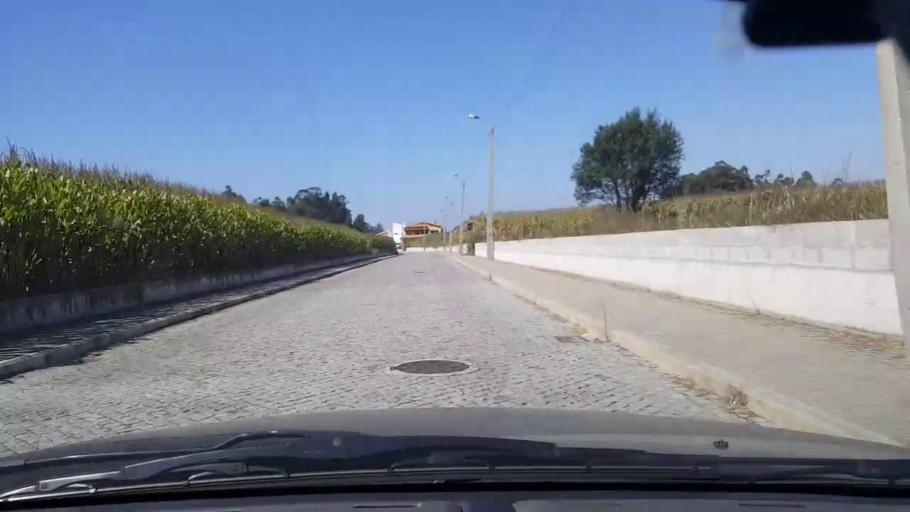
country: PT
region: Porto
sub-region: Vila do Conde
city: Arvore
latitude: 41.3028
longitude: -8.7129
